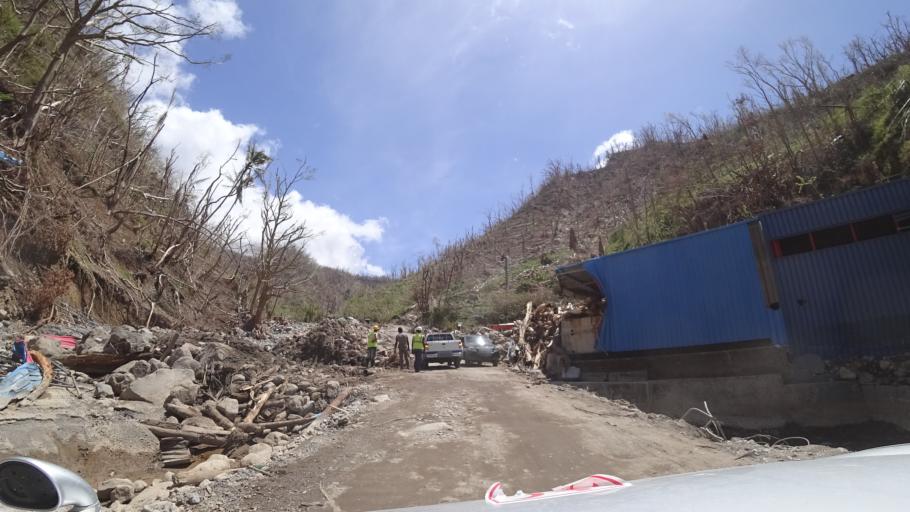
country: DM
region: Saint Luke
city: Pointe Michel
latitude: 15.2758
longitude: -61.3620
